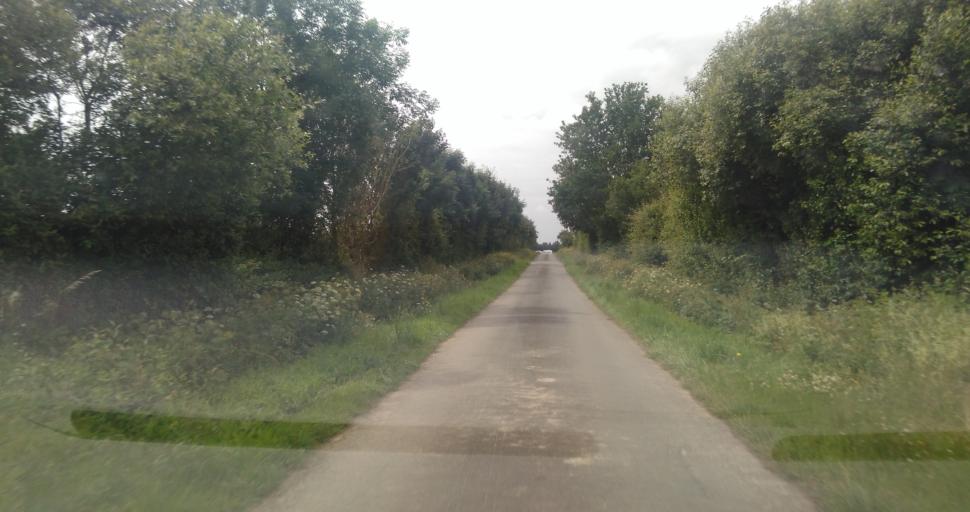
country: FR
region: Pays de la Loire
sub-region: Departement de la Vendee
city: Saint-Georges-de-Montaigu
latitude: 46.9292
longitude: -1.3210
